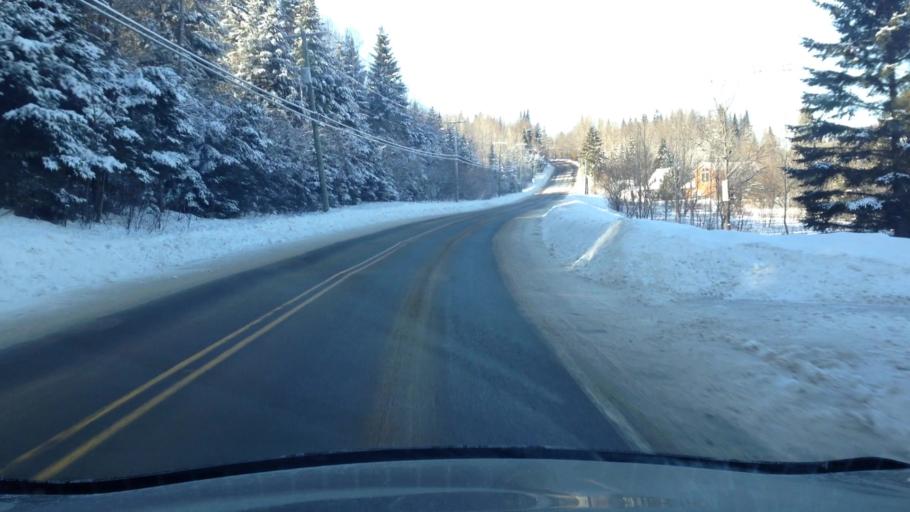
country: CA
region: Quebec
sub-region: Laurentides
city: Sainte-Agathe-des-Monts
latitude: 45.9322
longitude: -74.4324
